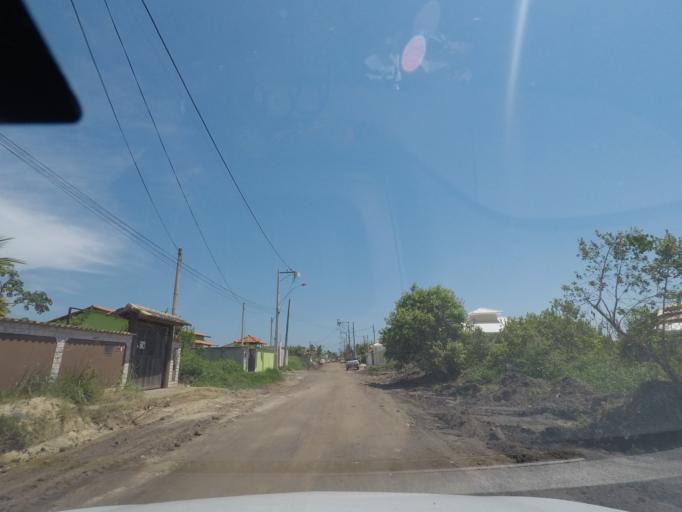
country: BR
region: Rio de Janeiro
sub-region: Marica
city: Marica
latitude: -22.9598
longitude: -42.9559
